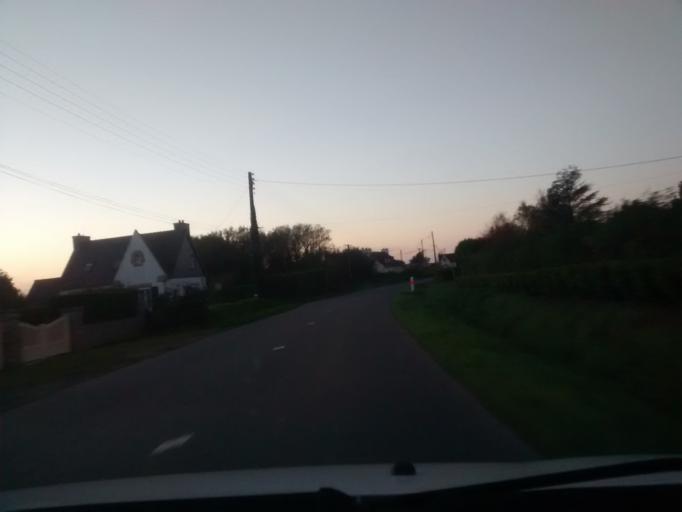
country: FR
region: Brittany
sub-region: Departement des Cotes-d'Armor
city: Trevou-Treguignec
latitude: 48.8098
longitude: -3.3305
